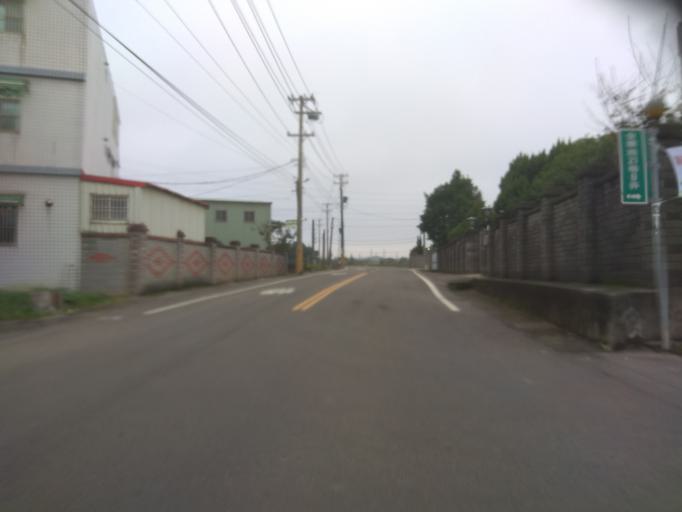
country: TW
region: Taiwan
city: Taoyuan City
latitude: 24.9971
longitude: 121.1235
